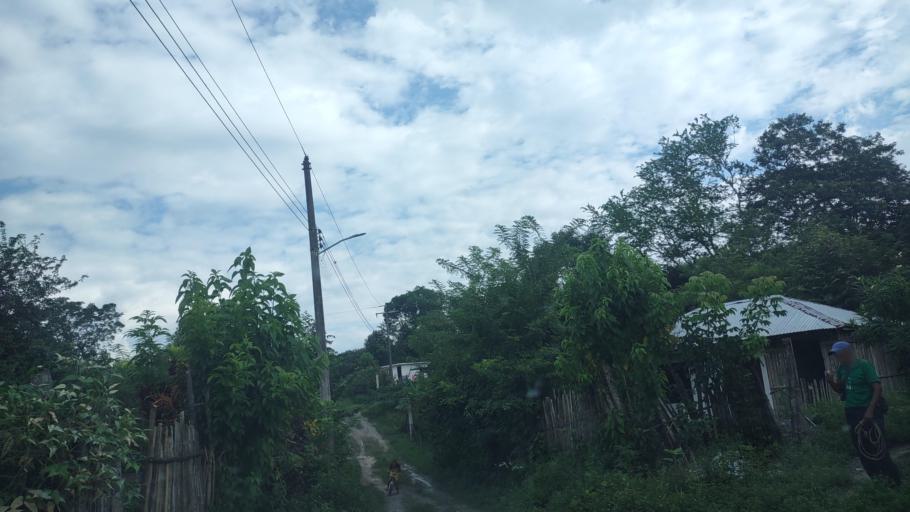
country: MX
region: Veracruz
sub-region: Ixcatepec
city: Ixcatepec
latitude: 21.2139
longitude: -97.9820
